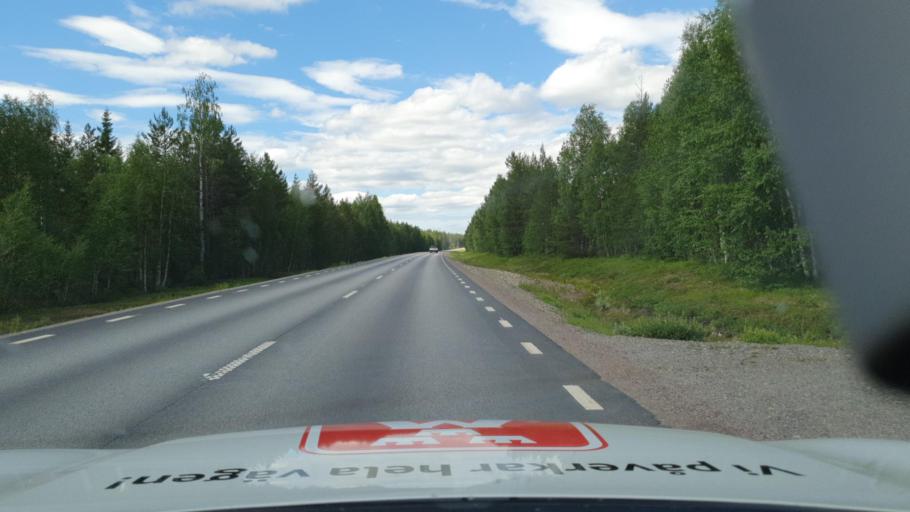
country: SE
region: Vaesterbotten
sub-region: Skelleftea Kommun
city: Langsele
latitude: 65.0708
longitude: 20.0266
